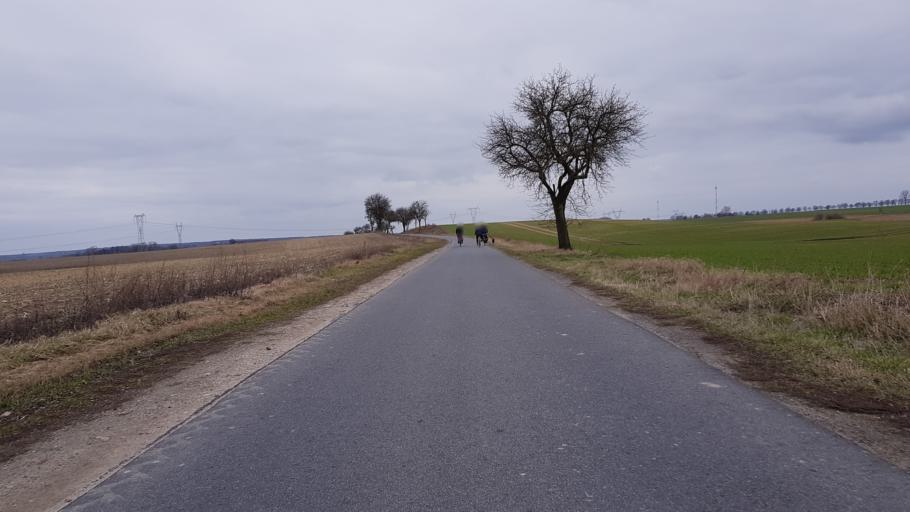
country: PL
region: West Pomeranian Voivodeship
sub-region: Powiat gryfinski
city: Banie
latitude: 53.0965
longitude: 14.6941
